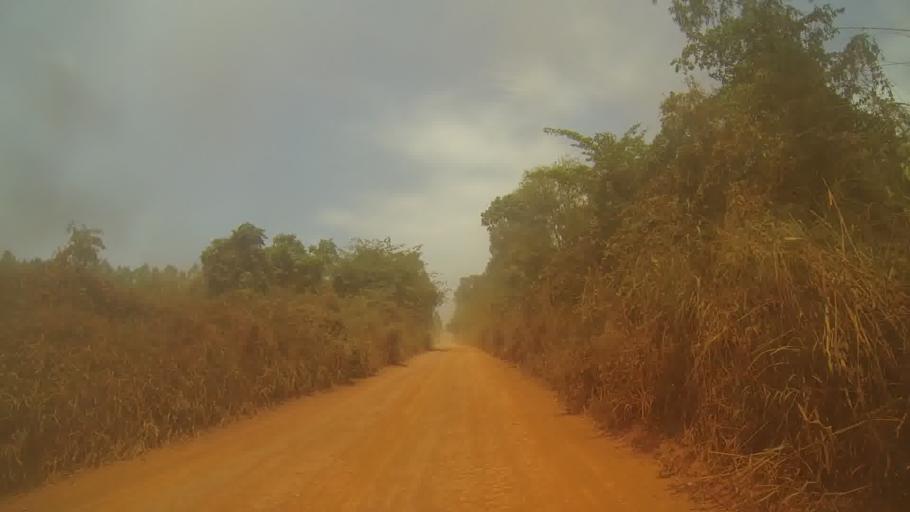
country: BR
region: Minas Gerais
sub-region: Bambui
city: Bambui
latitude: -20.0067
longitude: -45.9316
